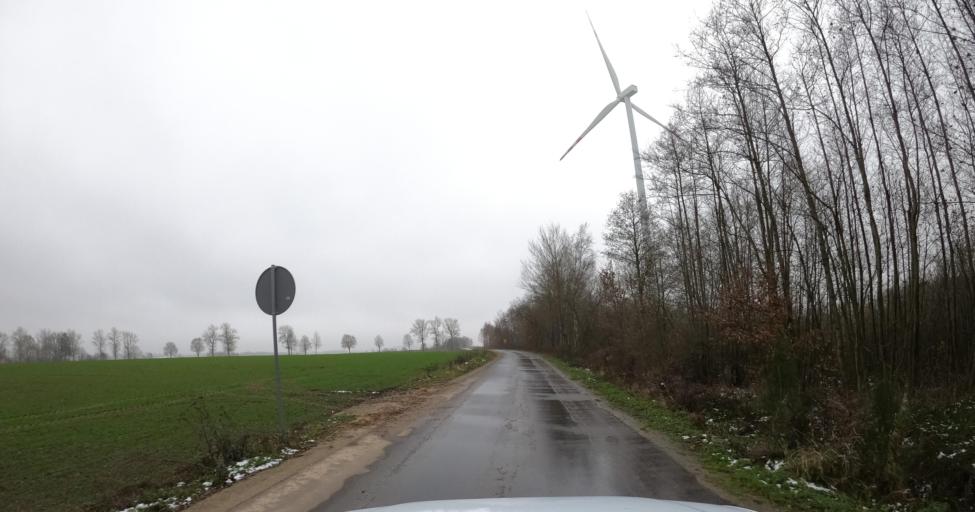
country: PL
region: West Pomeranian Voivodeship
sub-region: Powiat bialogardzki
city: Bialogard
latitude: 54.0326
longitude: 16.0347
